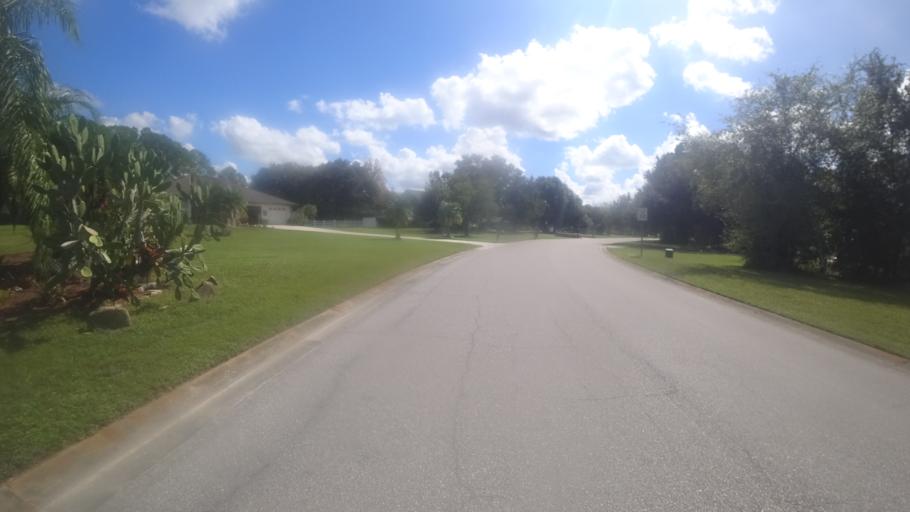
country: US
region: Florida
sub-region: Manatee County
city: Ellenton
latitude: 27.4908
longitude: -82.4042
